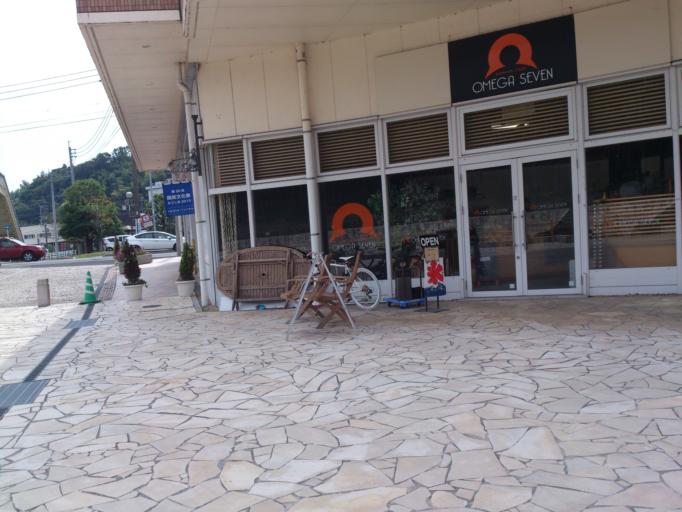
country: JP
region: Kagoshima
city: Kanoya
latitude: 31.3883
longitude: 130.8507
